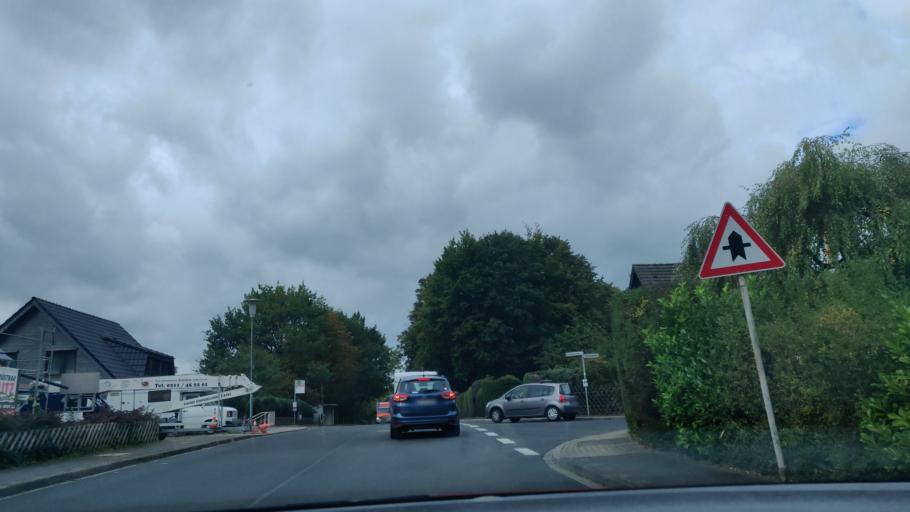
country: DE
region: North Rhine-Westphalia
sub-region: Regierungsbezirk Dusseldorf
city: Heiligenhaus
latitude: 51.2887
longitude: 6.9325
